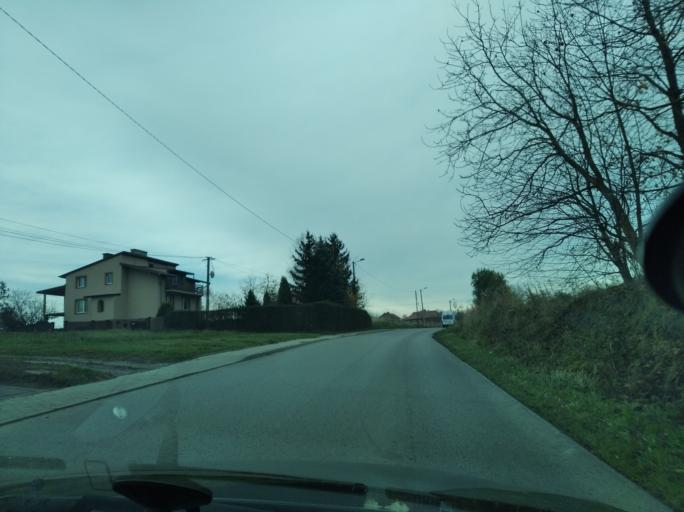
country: PL
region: Subcarpathian Voivodeship
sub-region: Powiat lancucki
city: Albigowa
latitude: 50.0323
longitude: 22.2373
